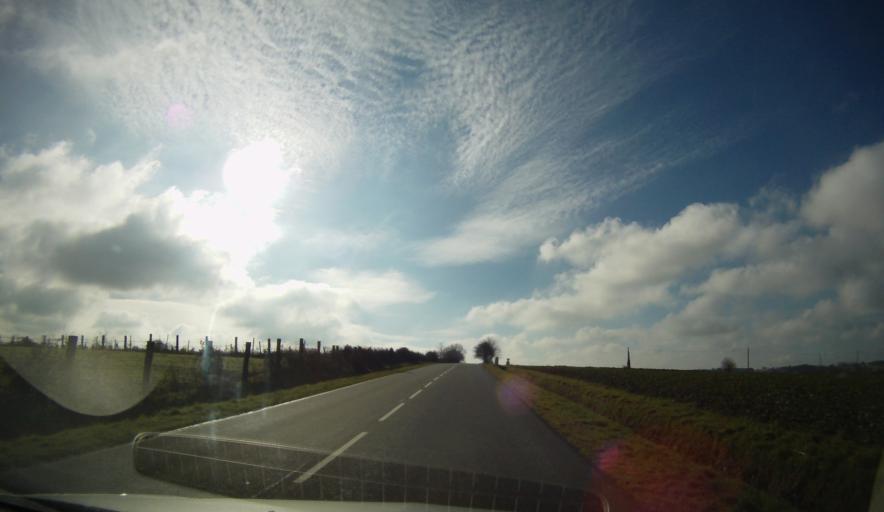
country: FR
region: Brittany
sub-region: Departement d'Ille-et-Vilaine
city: Corps-Nuds
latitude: 47.9377
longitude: -1.5592
